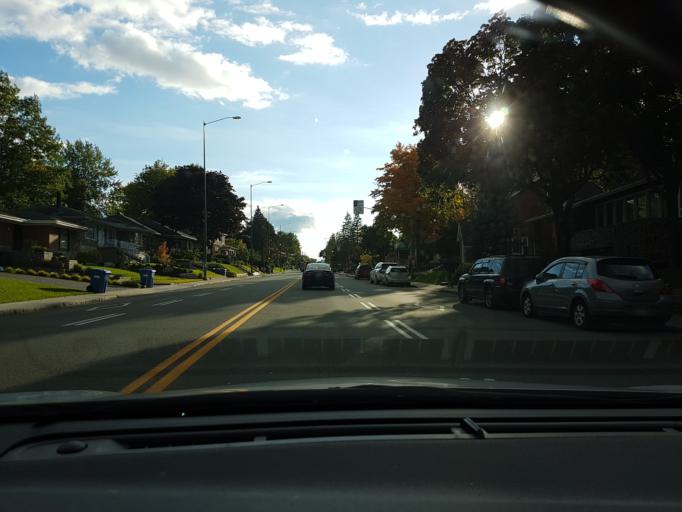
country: CA
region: Quebec
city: Quebec
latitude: 46.7885
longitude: -71.2545
